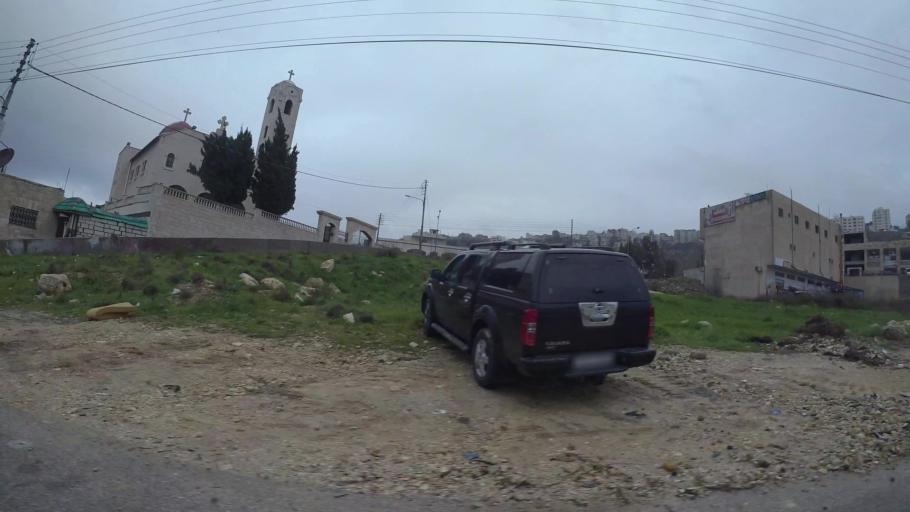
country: JO
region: Amman
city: Al Jubayhah
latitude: 32.0364
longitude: 35.8314
